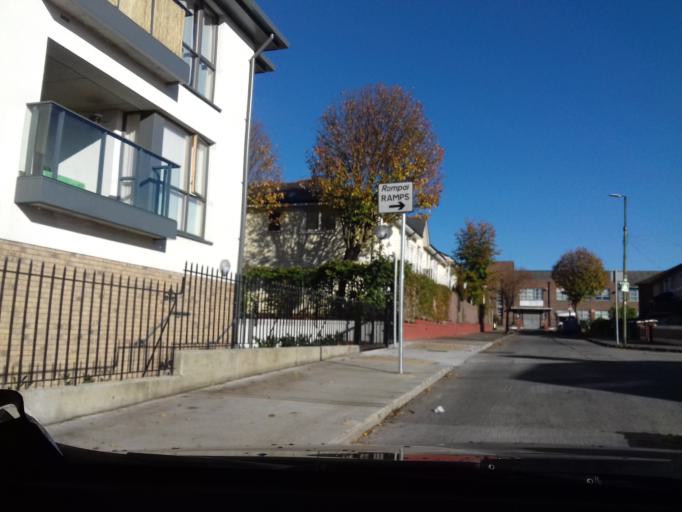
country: IE
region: Leinster
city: Cabra
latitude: 53.3677
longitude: -6.2945
